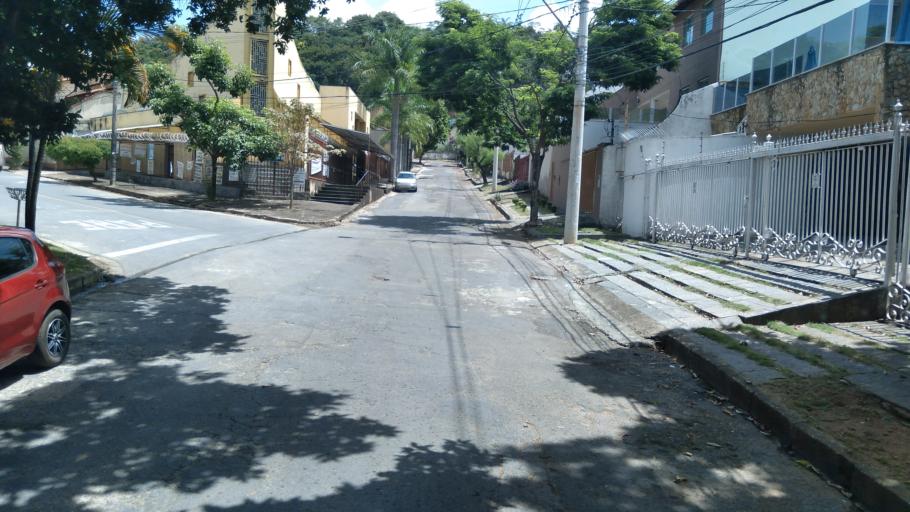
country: BR
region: Minas Gerais
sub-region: Contagem
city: Contagem
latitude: -19.9137
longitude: -44.0062
